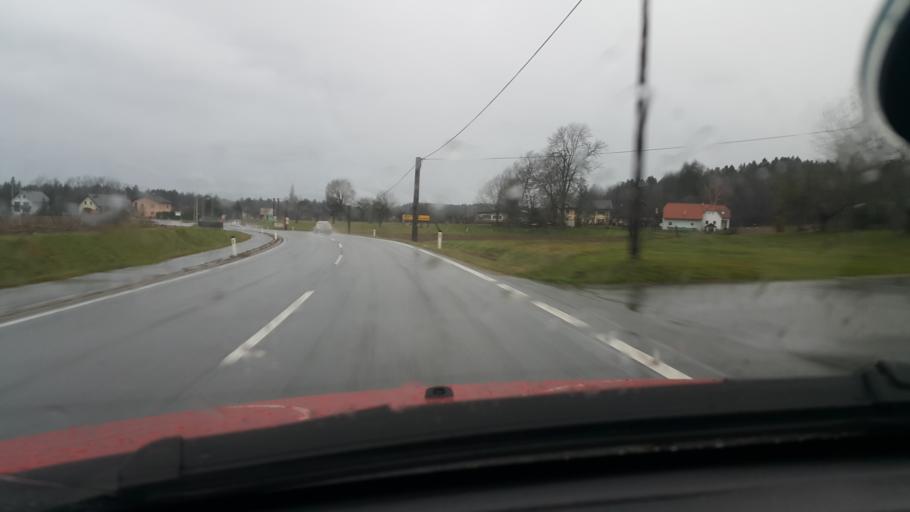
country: AT
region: Styria
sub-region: Politischer Bezirk Leibnitz
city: Hengsberg
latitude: 46.8651
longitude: 15.4577
